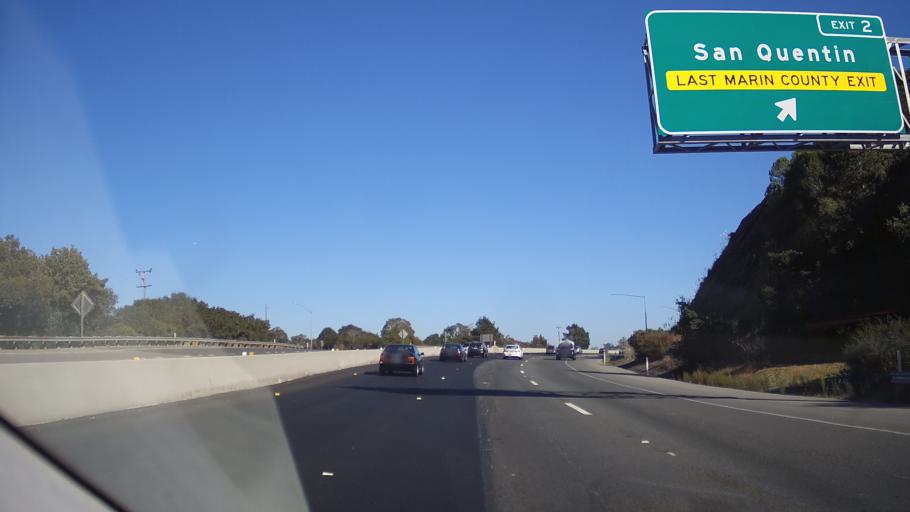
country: US
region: California
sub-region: Marin County
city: Corte Madera
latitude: 37.9449
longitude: -122.4853
